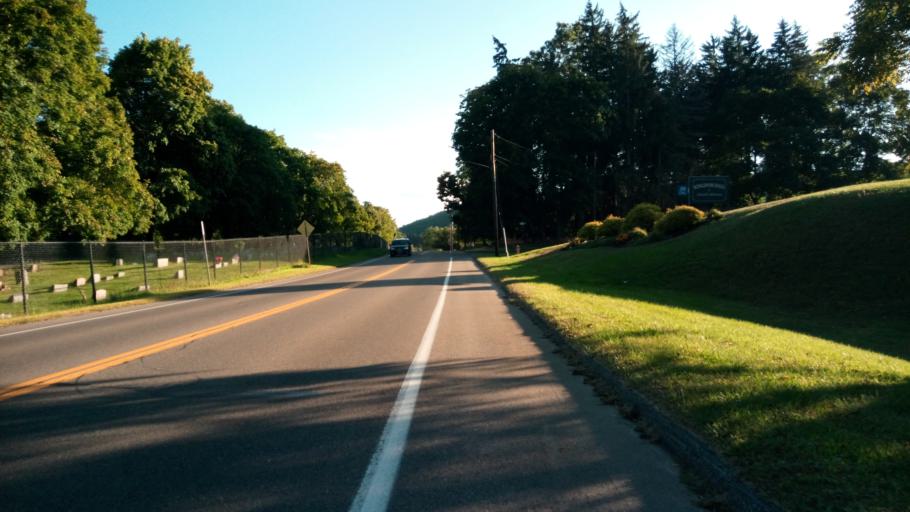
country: US
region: New York
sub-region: Chemung County
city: Elmira Heights
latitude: 42.1085
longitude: -76.8318
